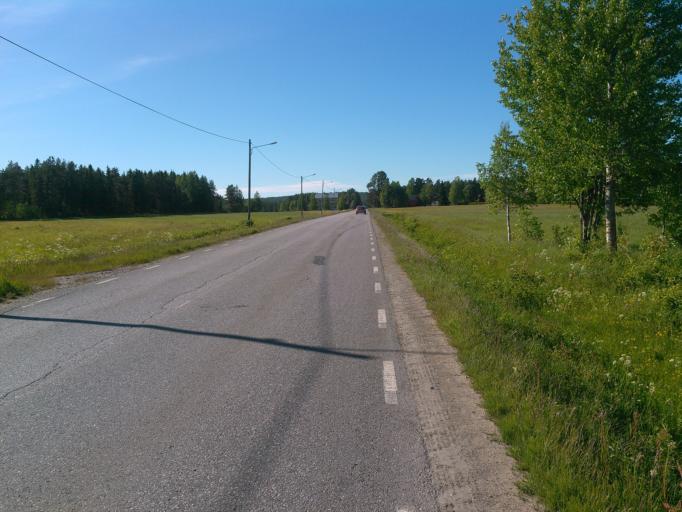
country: SE
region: Vaesterbotten
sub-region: Umea Kommun
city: Roback
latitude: 63.8271
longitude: 20.1193
